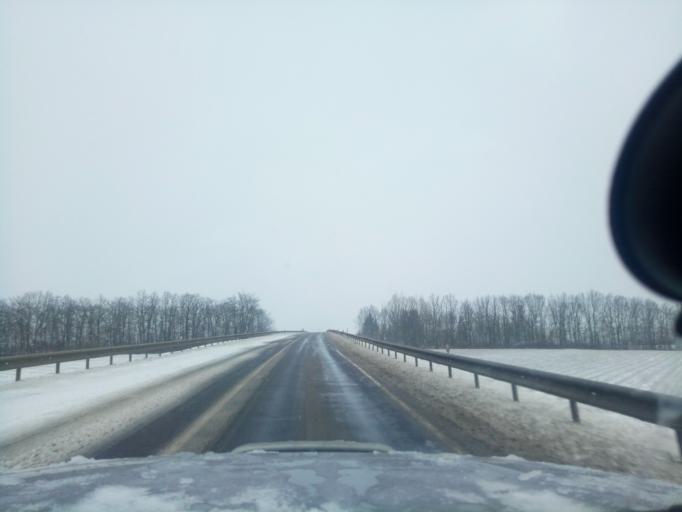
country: BY
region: Minsk
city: Haradzyeya
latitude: 53.3314
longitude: 26.5465
